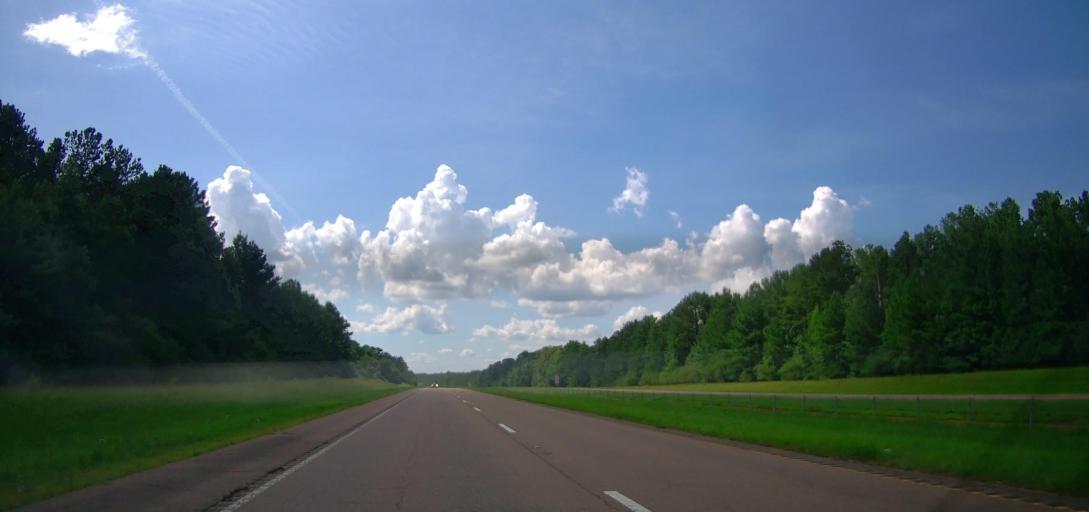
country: US
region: Mississippi
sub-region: Lowndes County
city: New Hope
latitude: 33.5012
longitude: -88.3065
